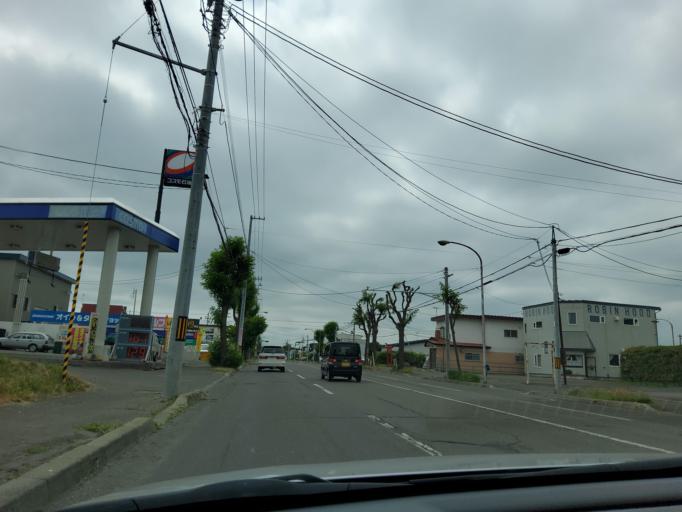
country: JP
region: Hokkaido
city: Obihiro
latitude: 42.9149
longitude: 143.1778
